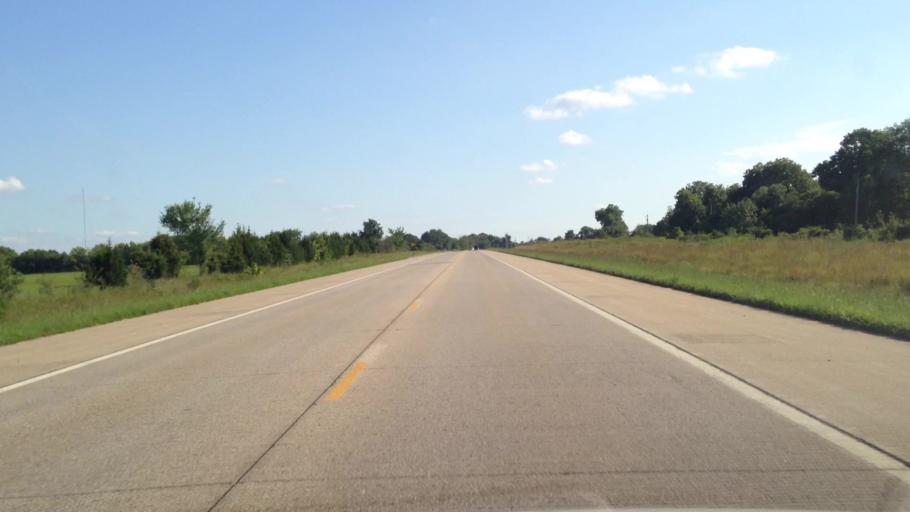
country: US
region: Kansas
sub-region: Crawford County
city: Arma
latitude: 37.5634
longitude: -94.7047
